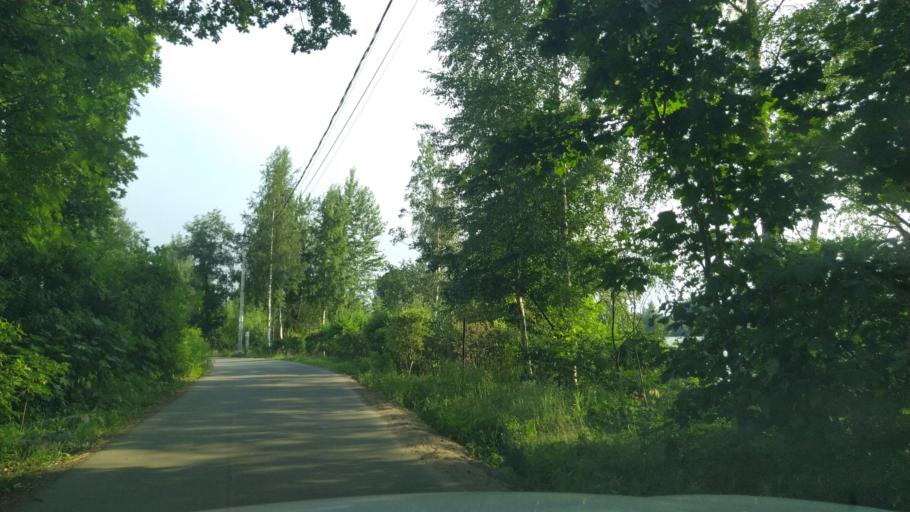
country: RU
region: Leningrad
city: Koltushi
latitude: 59.8943
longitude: 30.7330
